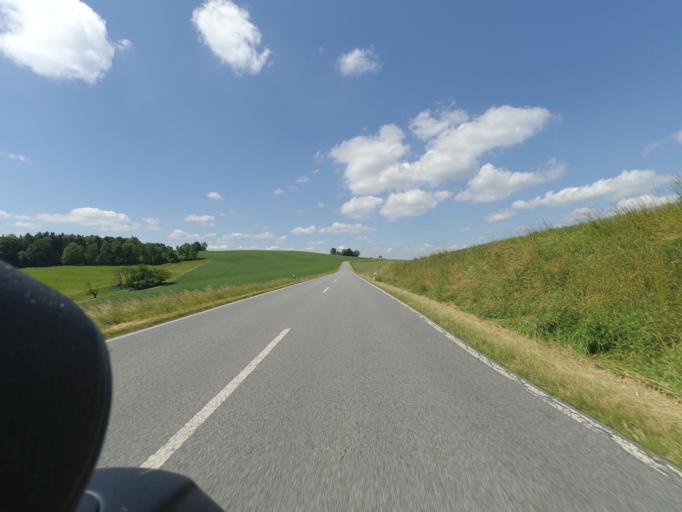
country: DE
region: Saxony
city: Sebnitz
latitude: 50.9412
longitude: 14.2247
